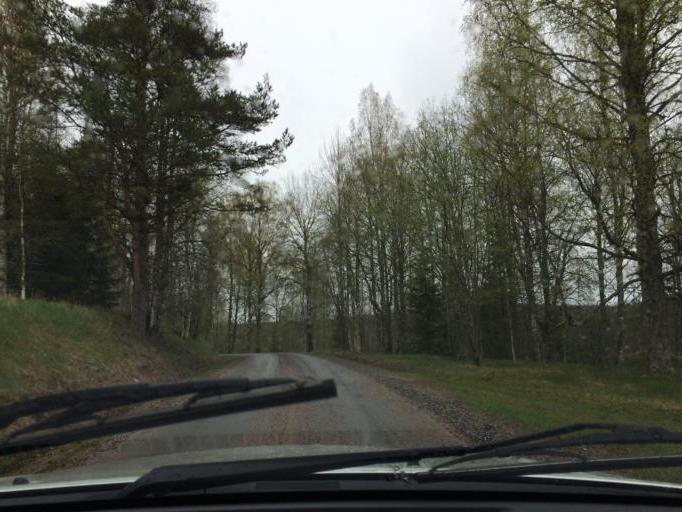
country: SE
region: Dalarna
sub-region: Ludvika Kommun
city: Abborrberget
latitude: 60.0214
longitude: 14.6303
